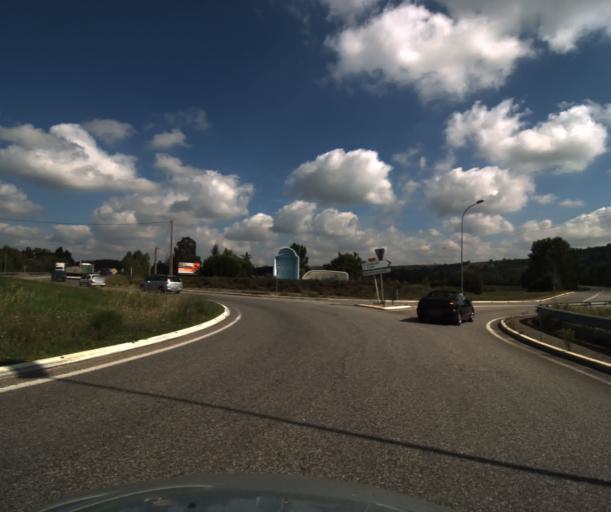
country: FR
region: Midi-Pyrenees
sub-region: Departement de la Haute-Garonne
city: Labarthe-sur-Leze
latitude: 43.4574
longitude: 1.4160
